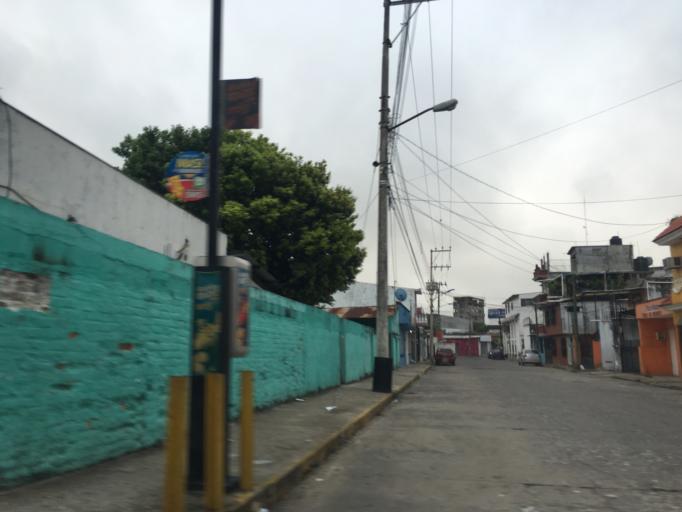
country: MX
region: Tabasco
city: Villahermosa
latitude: 17.9836
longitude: -92.9490
